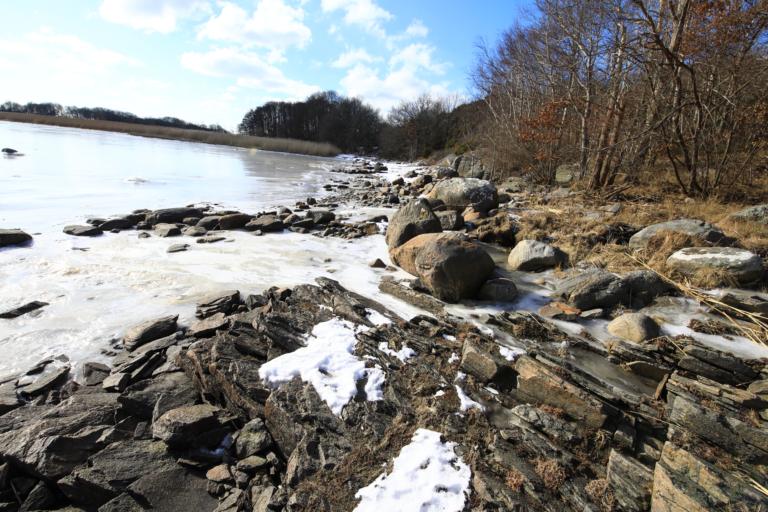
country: SE
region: Halland
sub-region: Kungsbacka Kommun
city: Frillesas
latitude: 57.2185
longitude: 12.1833
